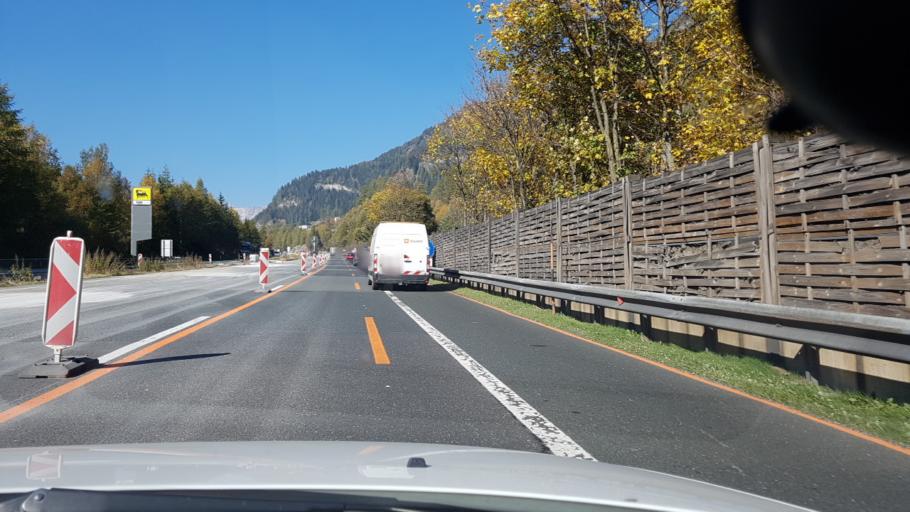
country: AT
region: Salzburg
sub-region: Politischer Bezirk Tamsweg
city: Zederhaus
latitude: 47.1324
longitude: 13.5480
